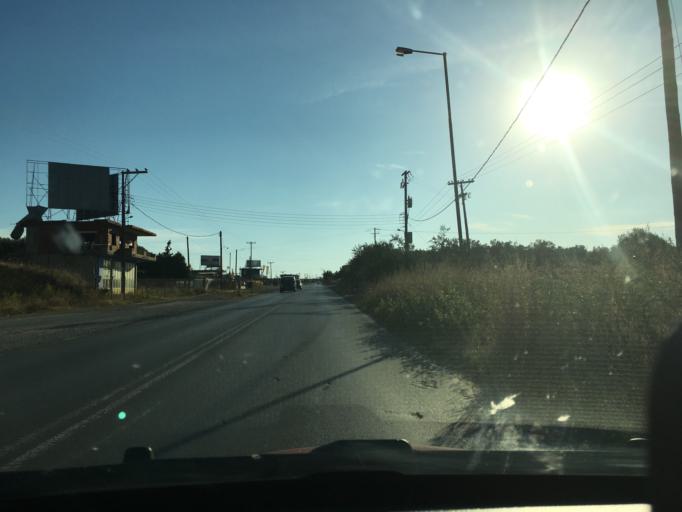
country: GR
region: Central Macedonia
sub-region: Nomos Chalkidikis
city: Olynthos
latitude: 40.2619
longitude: 23.3313
